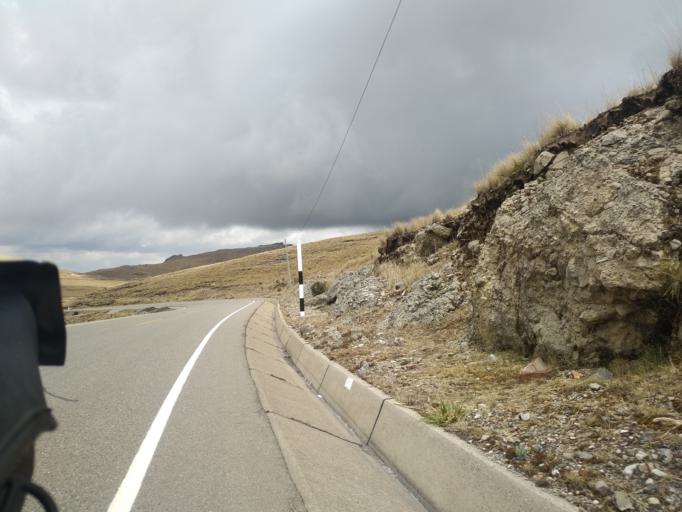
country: PE
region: La Libertad
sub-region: Provincia de Santiago de Chuco
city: Quiruvilca
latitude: -7.9422
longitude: -78.1874
